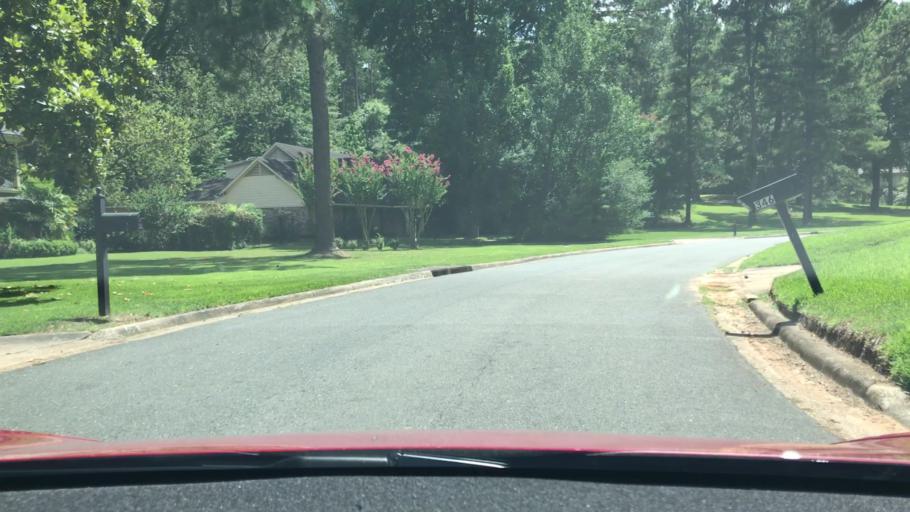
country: US
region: Louisiana
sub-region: Bossier Parish
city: Bossier City
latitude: 32.4323
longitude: -93.7313
